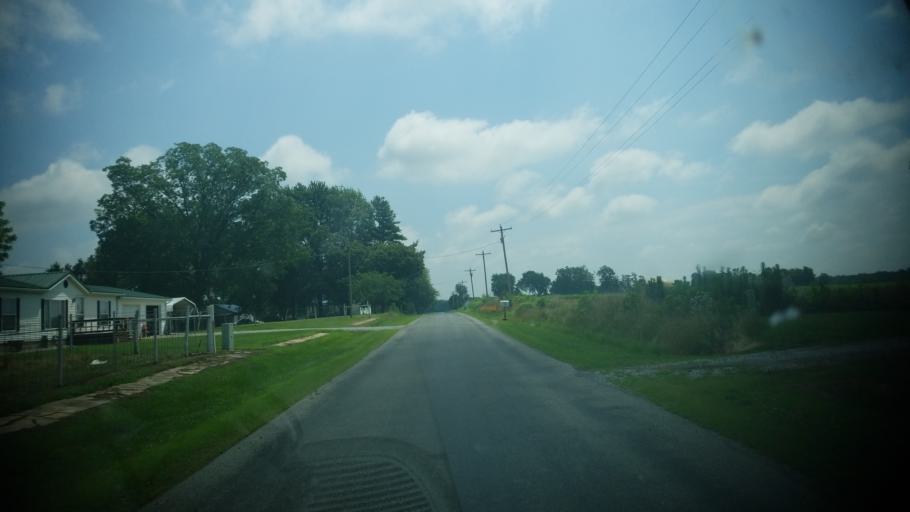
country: US
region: Illinois
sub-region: Wayne County
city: Fairfield
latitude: 38.5223
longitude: -88.3544
